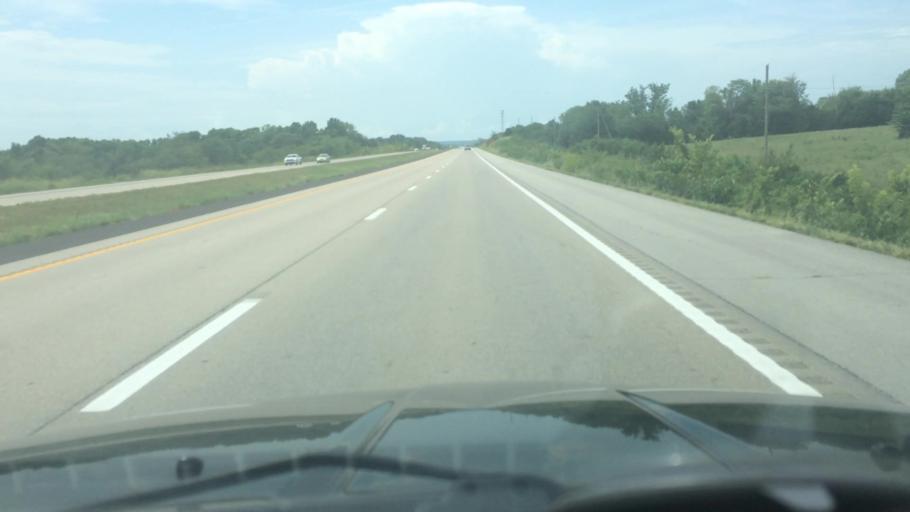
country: US
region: Missouri
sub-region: Polk County
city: Humansville
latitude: 37.7710
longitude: -93.5658
